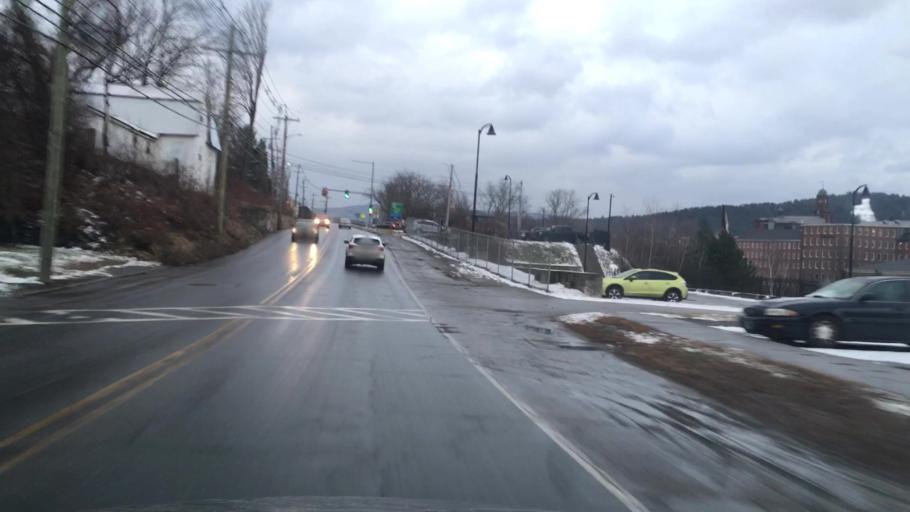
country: US
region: New Hampshire
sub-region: Sullivan County
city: Claremont
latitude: 43.3766
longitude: -72.3399
